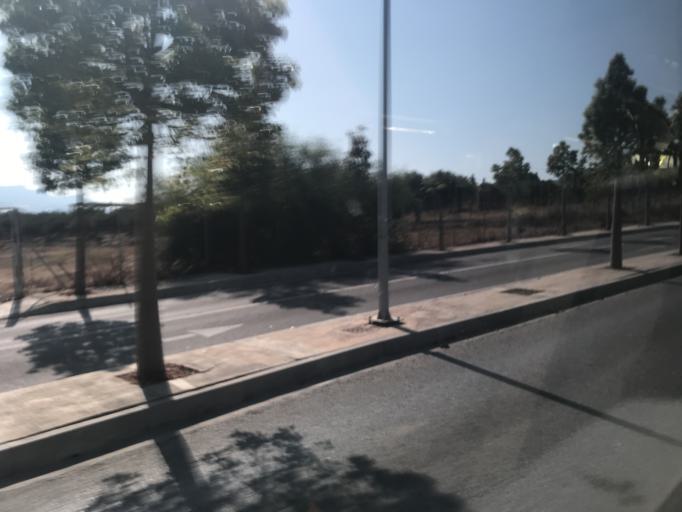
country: GR
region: Crete
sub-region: Nomos Irakleiou
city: Gazi
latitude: 35.3026
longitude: 25.0842
